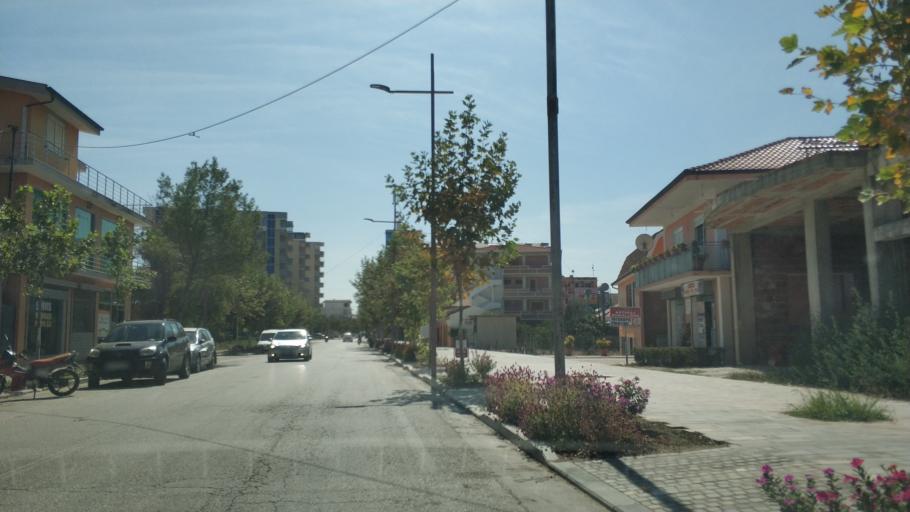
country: AL
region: Fier
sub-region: Rrethi i Lushnjes
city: Divjake
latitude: 40.9977
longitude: 19.5322
